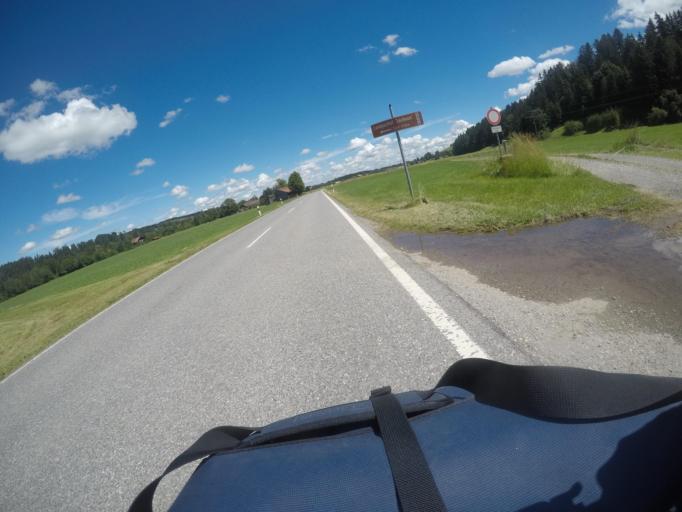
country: DE
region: Bavaria
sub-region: Upper Bavaria
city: Prem
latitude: 47.6640
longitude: 10.7857
